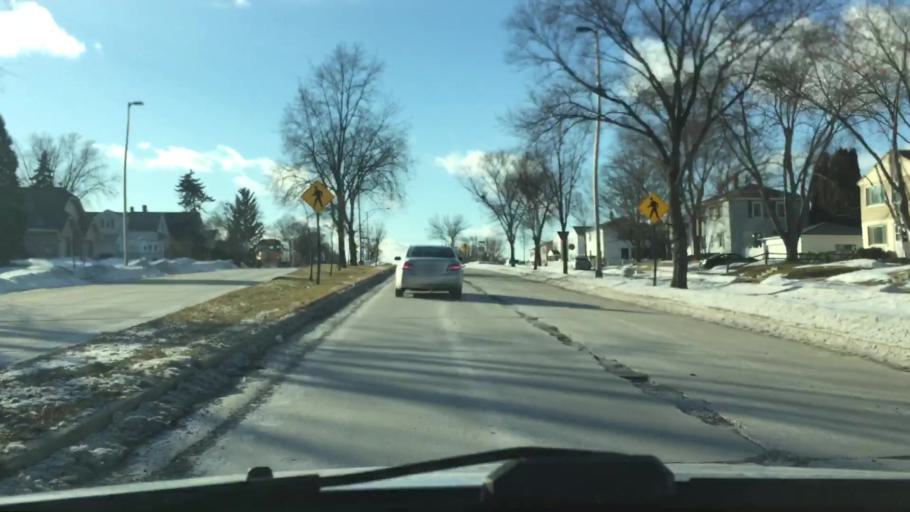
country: US
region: Wisconsin
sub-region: Milwaukee County
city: West Milwaukee
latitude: 42.9739
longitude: -87.9731
